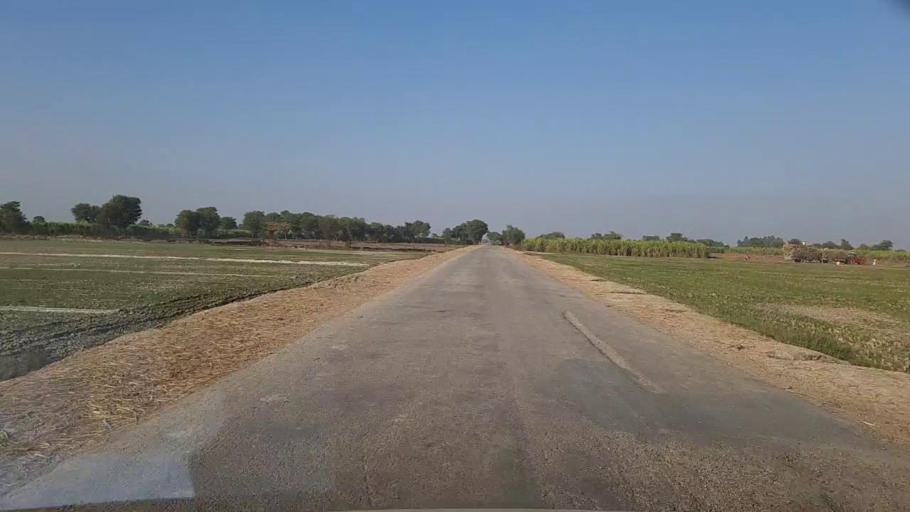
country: PK
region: Sindh
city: Dadu
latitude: 26.8470
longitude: 67.7937
